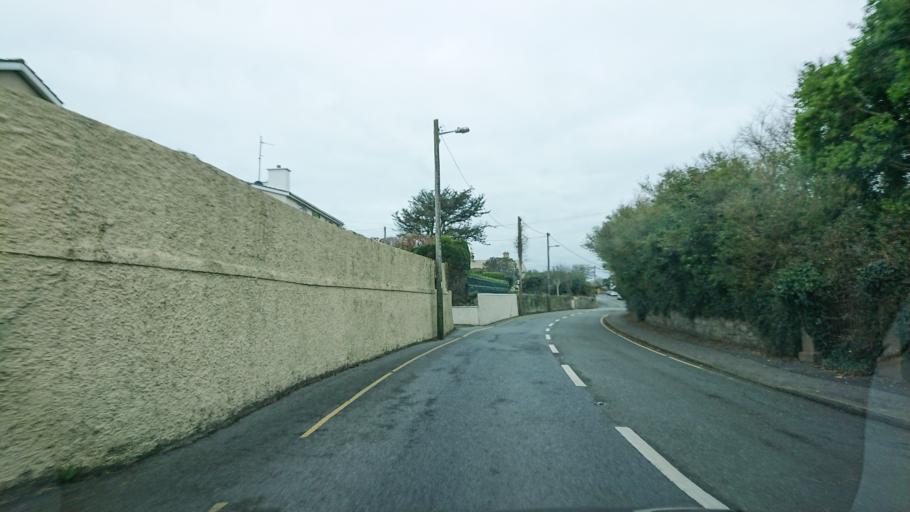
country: IE
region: Munster
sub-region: Waterford
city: Tra Mhor
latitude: 52.1546
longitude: -7.1617
